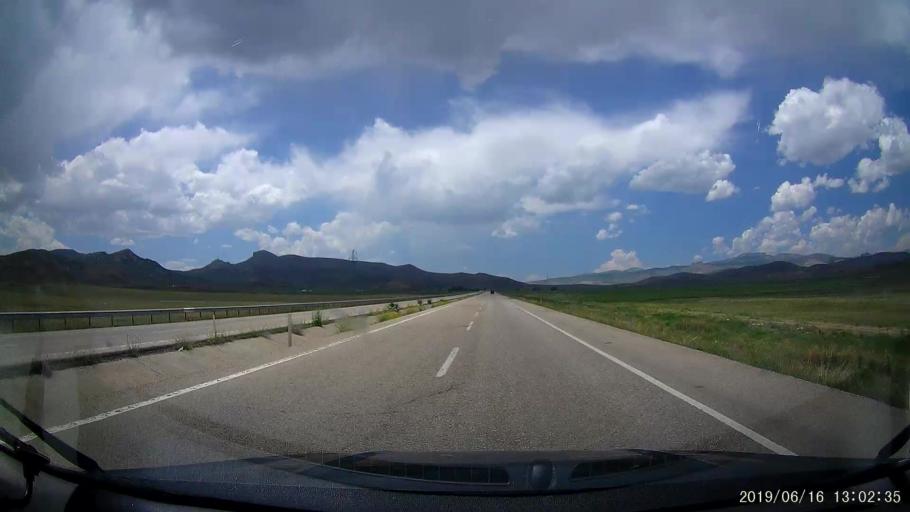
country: TR
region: Agri
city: Sulucem
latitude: 39.5755
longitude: 43.8121
